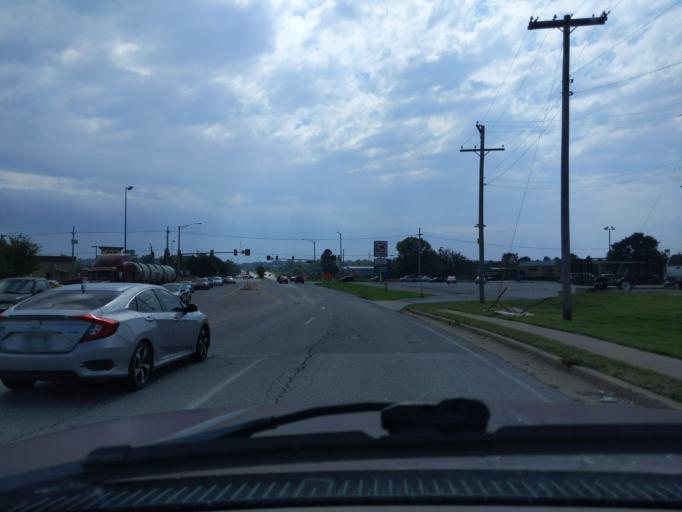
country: US
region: Oklahoma
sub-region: Tulsa County
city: Sand Springs
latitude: 36.1348
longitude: -96.1158
